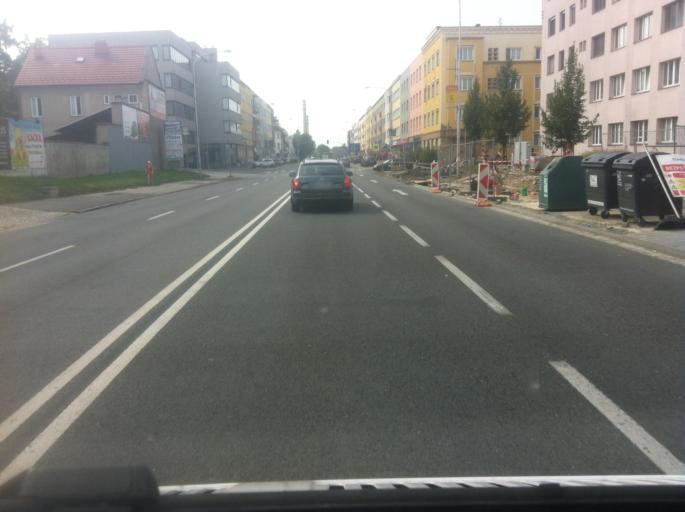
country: CZ
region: Zlin
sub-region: Okres Zlin
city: Zlin
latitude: 49.2256
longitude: 17.6737
